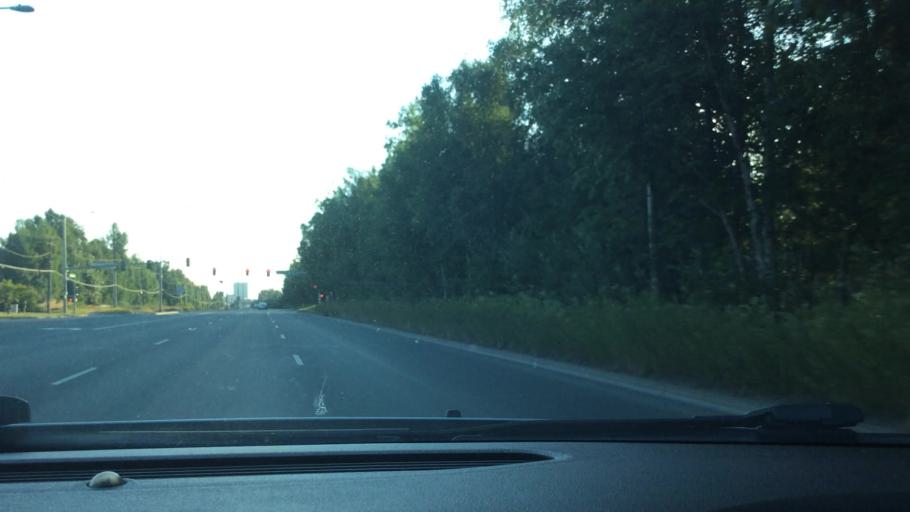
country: US
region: Alaska
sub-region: Anchorage Municipality
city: Anchorage
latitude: 61.1955
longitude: -149.8430
